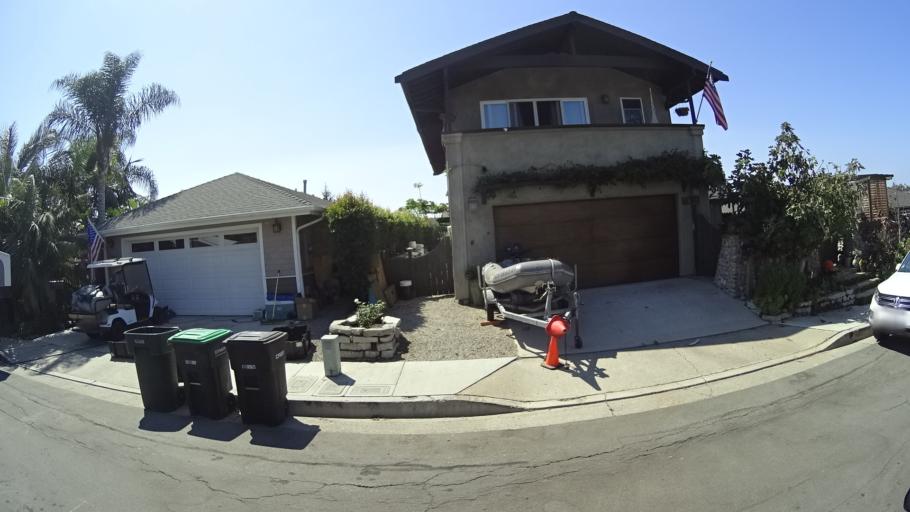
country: US
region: California
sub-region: Orange County
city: San Clemente
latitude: 33.4444
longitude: -117.6402
